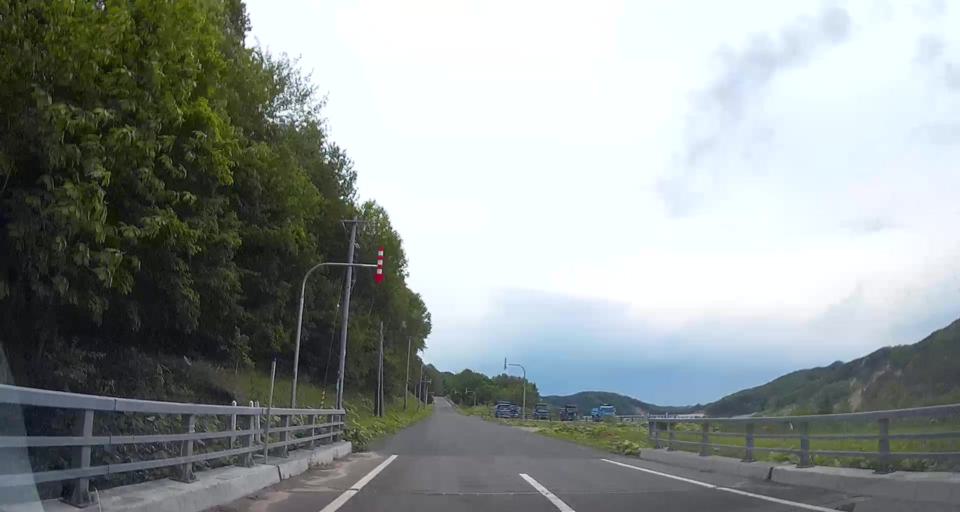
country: JP
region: Hokkaido
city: Chitose
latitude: 42.7763
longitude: 142.0094
